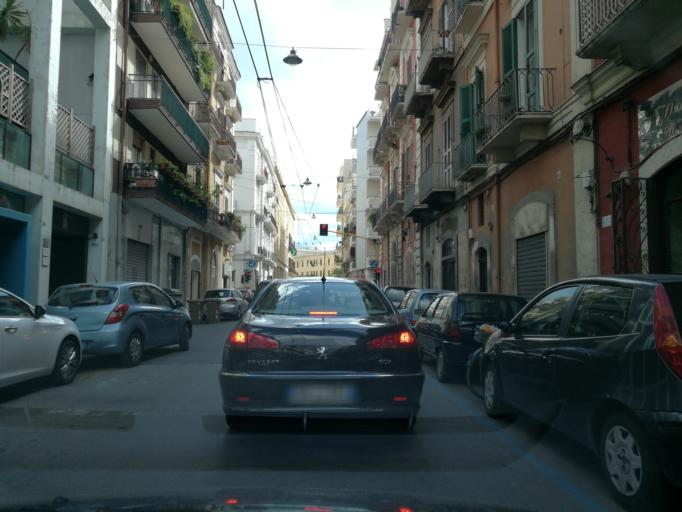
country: IT
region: Apulia
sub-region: Provincia di Bari
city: Bari
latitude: 41.1268
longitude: 16.8620
